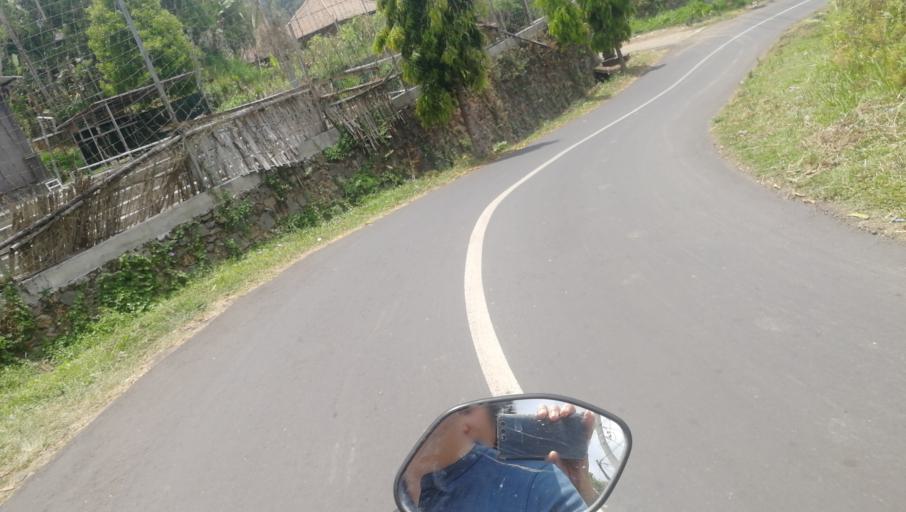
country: ID
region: Bali
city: Banjar Pedawa
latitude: -8.2637
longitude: 115.0304
